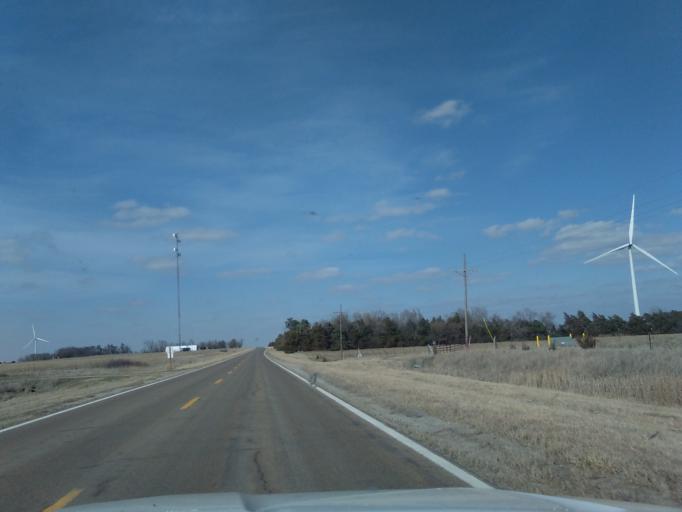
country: US
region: Nebraska
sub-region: Jefferson County
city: Fairbury
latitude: 40.0513
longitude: -96.9351
